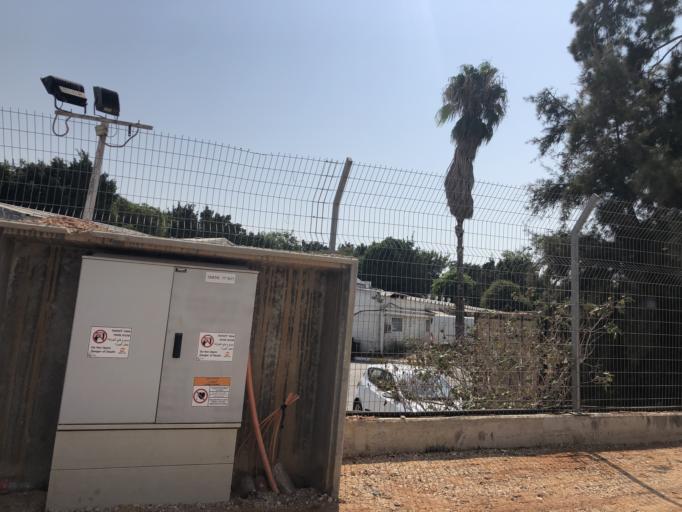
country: IL
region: Tel Aviv
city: Giv`atayim
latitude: 32.0567
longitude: 34.8282
